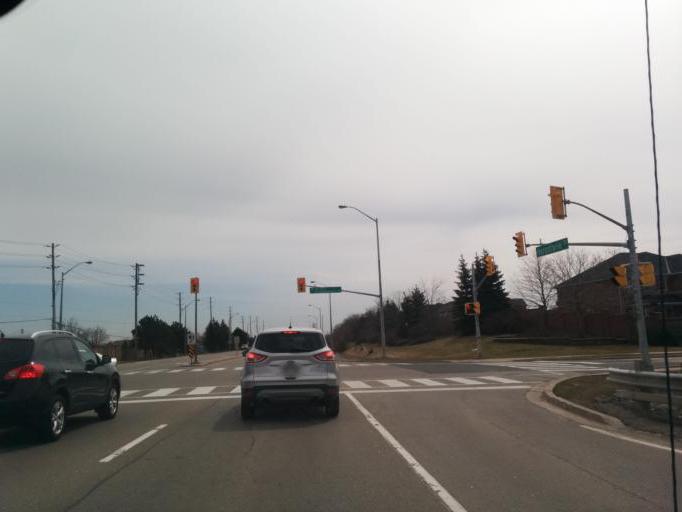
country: CA
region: Ontario
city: Brampton
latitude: 43.7283
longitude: -79.8176
